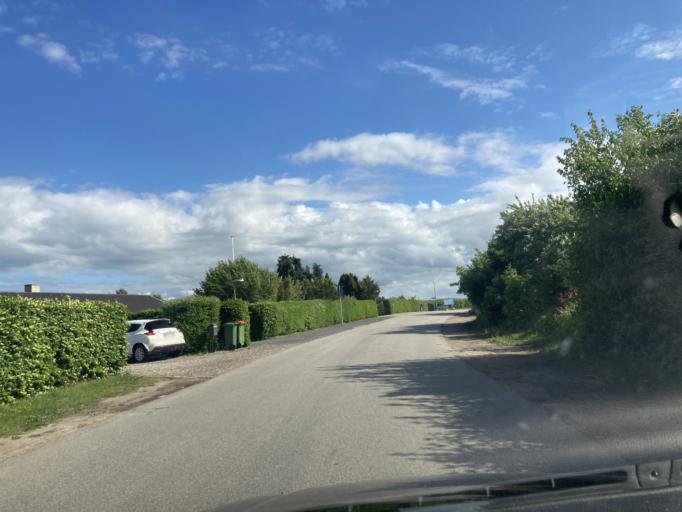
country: DK
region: Capital Region
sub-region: Gribskov Kommune
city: Helsinge
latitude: 56.0135
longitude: 12.1111
